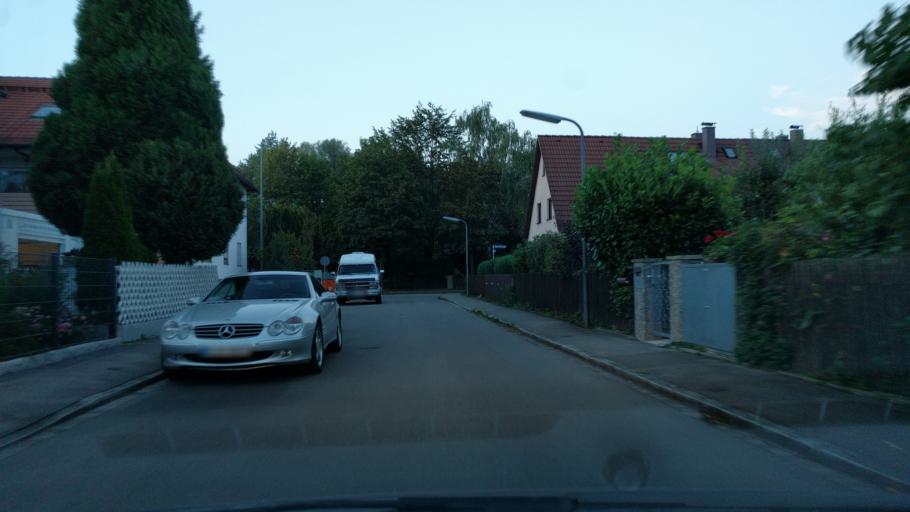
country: DE
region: Bavaria
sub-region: Upper Bavaria
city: Neubiberg
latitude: 48.1303
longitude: 11.6665
